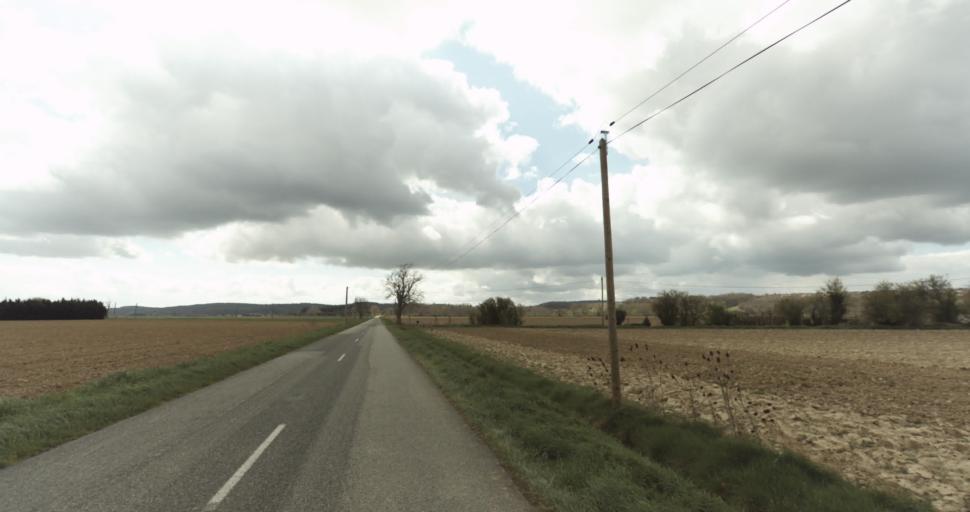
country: FR
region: Midi-Pyrenees
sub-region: Departement de la Haute-Garonne
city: Auterive
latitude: 43.3152
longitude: 1.4741
